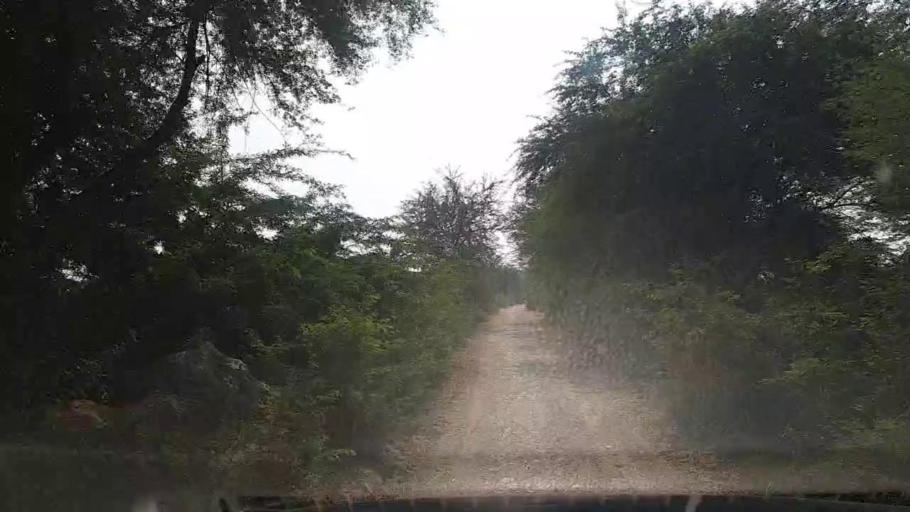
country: PK
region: Sindh
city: Mirpur Batoro
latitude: 24.6877
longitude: 68.2218
